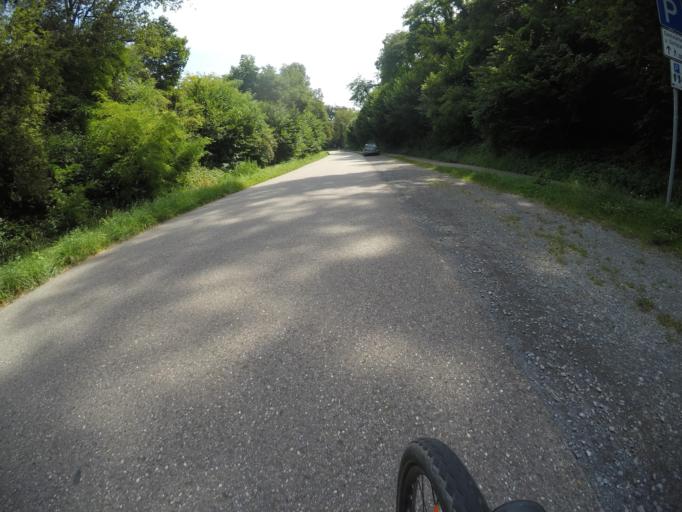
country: DE
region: Baden-Wuerttemberg
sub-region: Karlsruhe Region
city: Bruchsal
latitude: 49.1074
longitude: 8.6040
